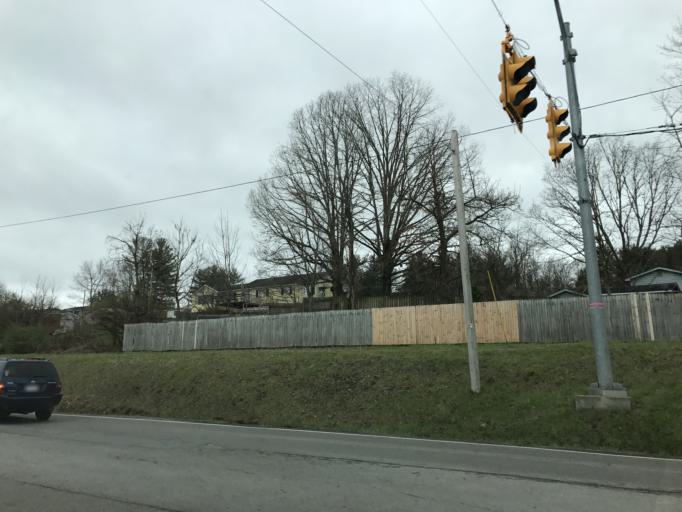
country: US
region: West Virginia
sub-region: Raleigh County
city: Beckley
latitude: 37.7979
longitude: -81.1766
